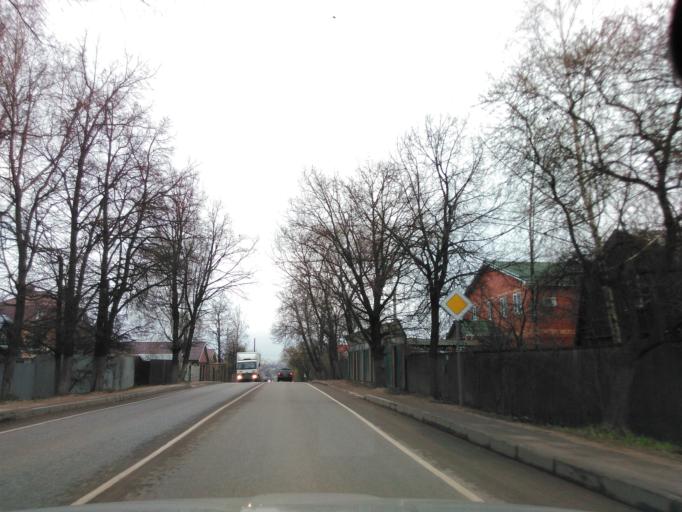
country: RU
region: Moskovskaya
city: Pavlovskaya Sloboda
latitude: 55.8146
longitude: 37.0788
